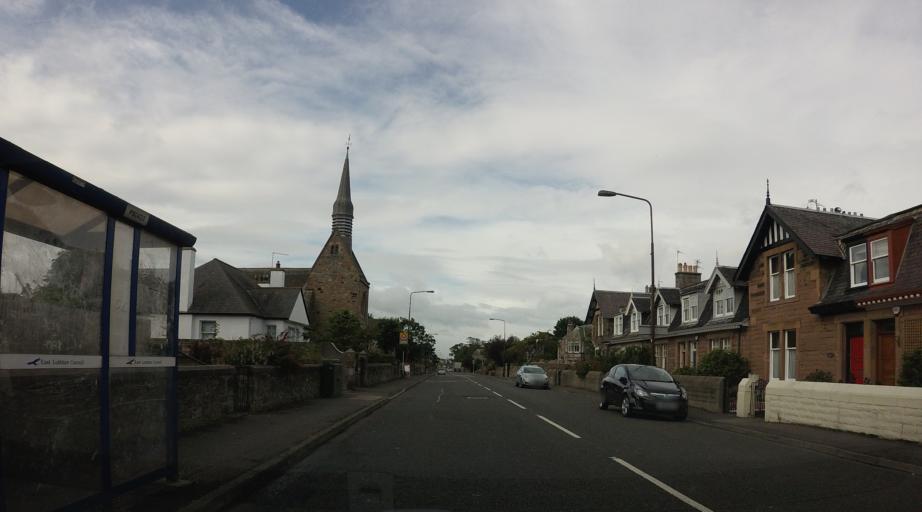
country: GB
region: Scotland
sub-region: East Lothian
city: Cockenzie
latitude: 55.9706
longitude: -2.9567
